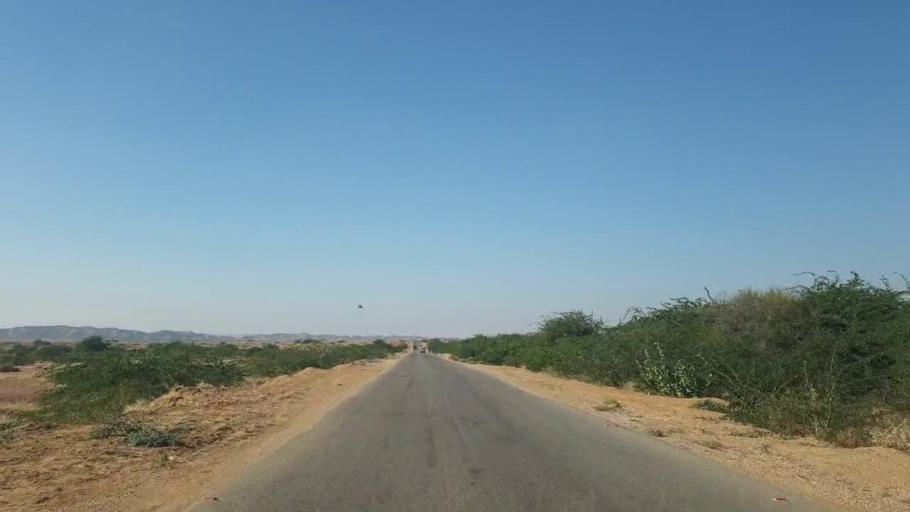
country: PK
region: Sindh
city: Malir Cantonment
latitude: 25.2769
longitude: 67.5877
